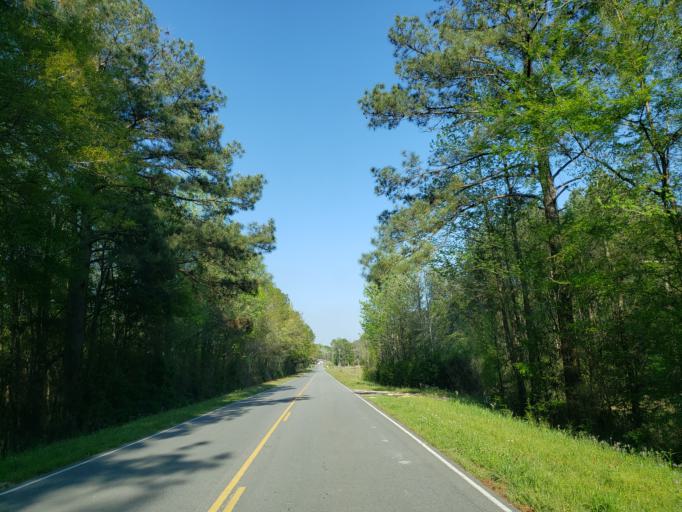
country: US
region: Mississippi
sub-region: Perry County
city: Richton
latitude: 31.4809
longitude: -89.0419
